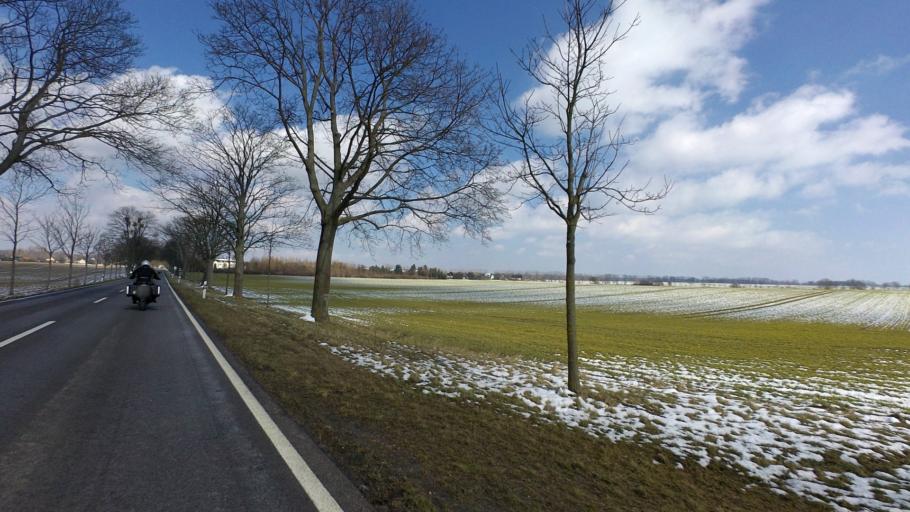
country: DE
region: Brandenburg
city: Eberswalde
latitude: 52.7652
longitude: 13.8397
